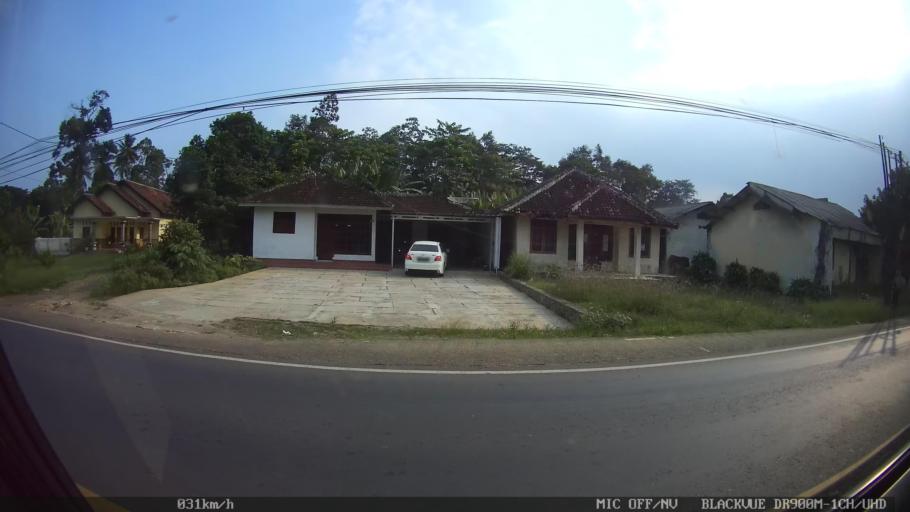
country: ID
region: Lampung
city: Natar
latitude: -5.3694
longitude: 105.1734
